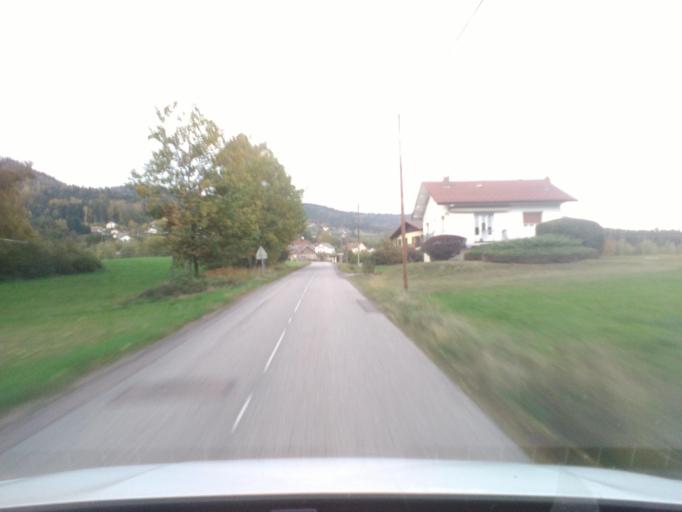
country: FR
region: Lorraine
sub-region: Departement des Vosges
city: Saint-Ame
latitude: 48.0377
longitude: 6.6722
